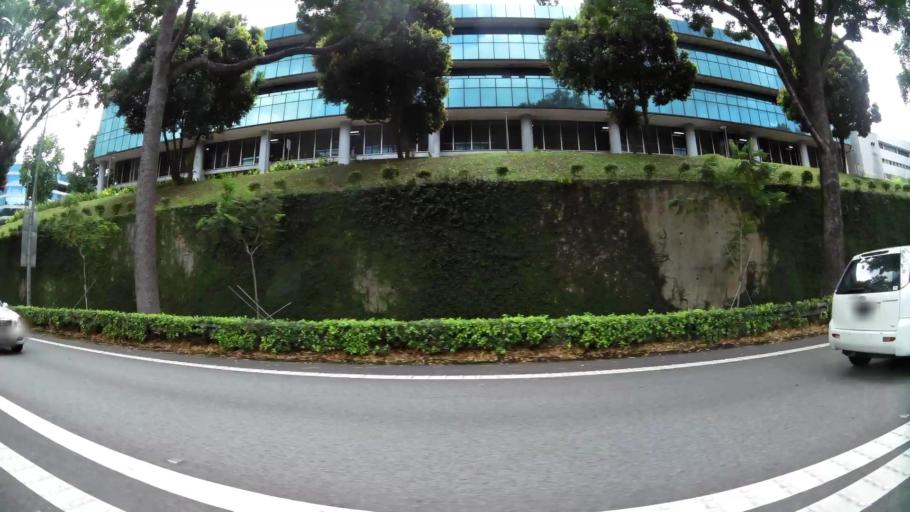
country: SG
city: Singapore
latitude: 1.2905
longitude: 103.7906
